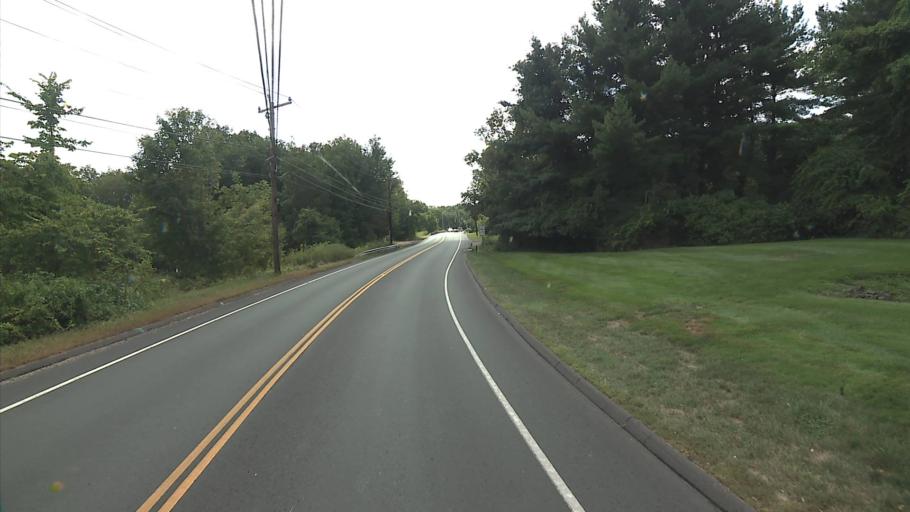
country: US
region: Connecticut
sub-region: Hartford County
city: Weatogue
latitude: 41.8299
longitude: -72.7714
